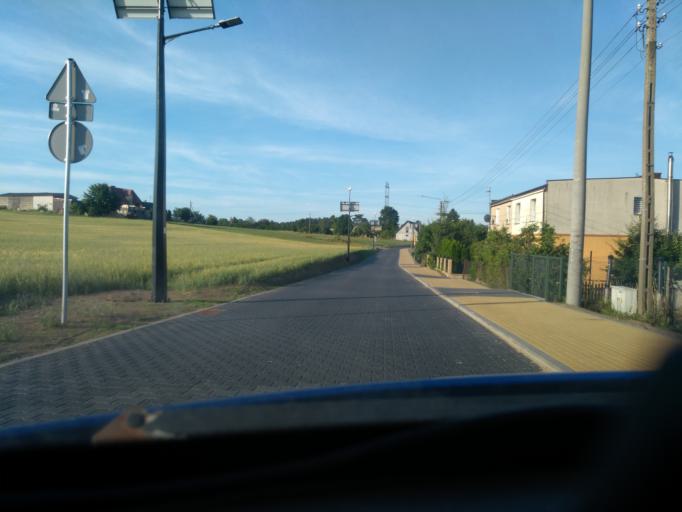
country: PL
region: Pomeranian Voivodeship
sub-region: Powiat kartuski
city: Przodkowo
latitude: 54.3975
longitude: 18.3306
